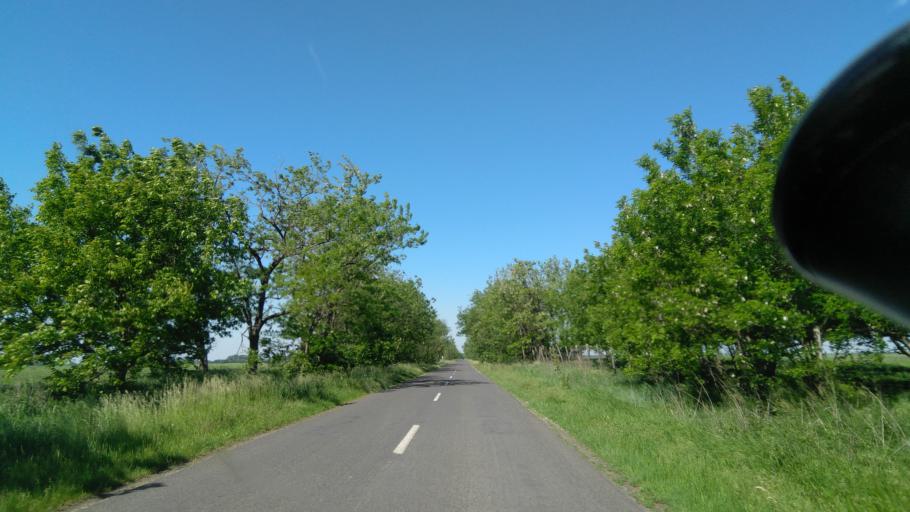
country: HU
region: Bekes
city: Kevermes
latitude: 46.4260
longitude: 21.1544
